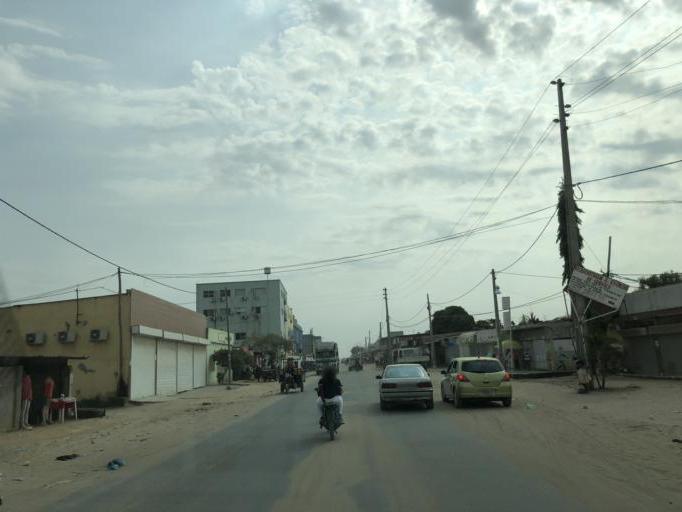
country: AO
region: Luanda
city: Luanda
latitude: -8.9063
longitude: 13.3434
